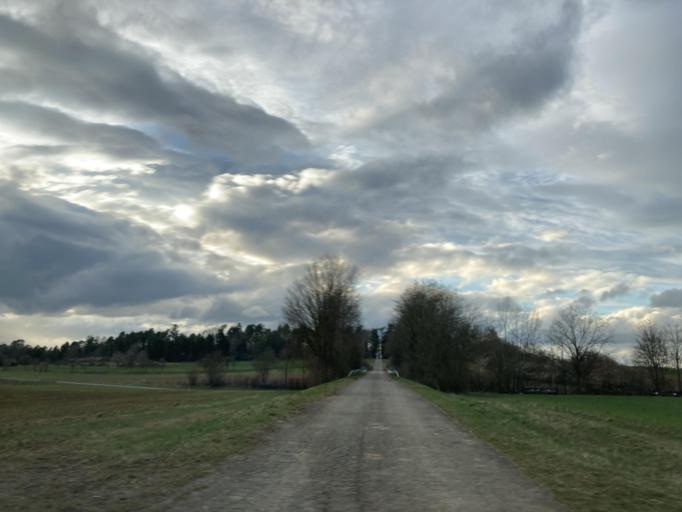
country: DE
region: Baden-Wuerttemberg
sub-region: Tuebingen Region
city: Rottenburg
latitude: 48.4978
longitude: 8.8897
